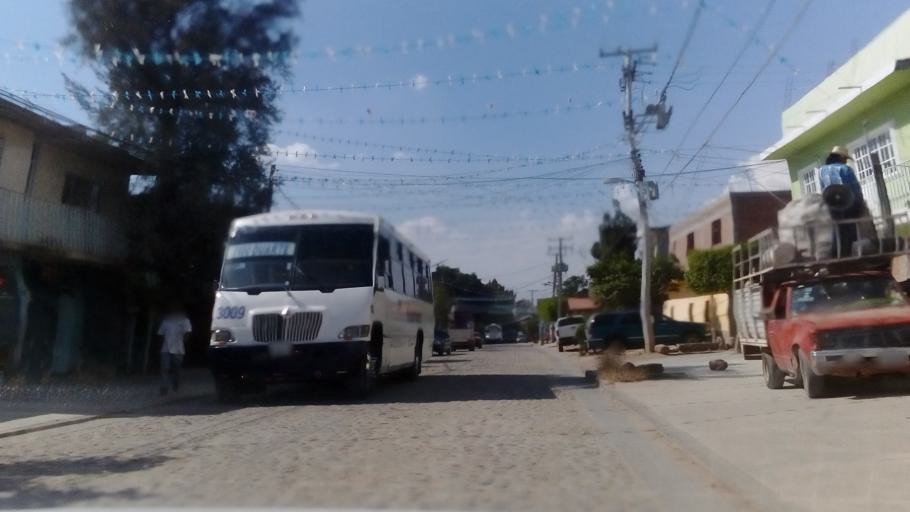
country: MX
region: Guanajuato
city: Duarte
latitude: 21.0843
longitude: -101.5169
